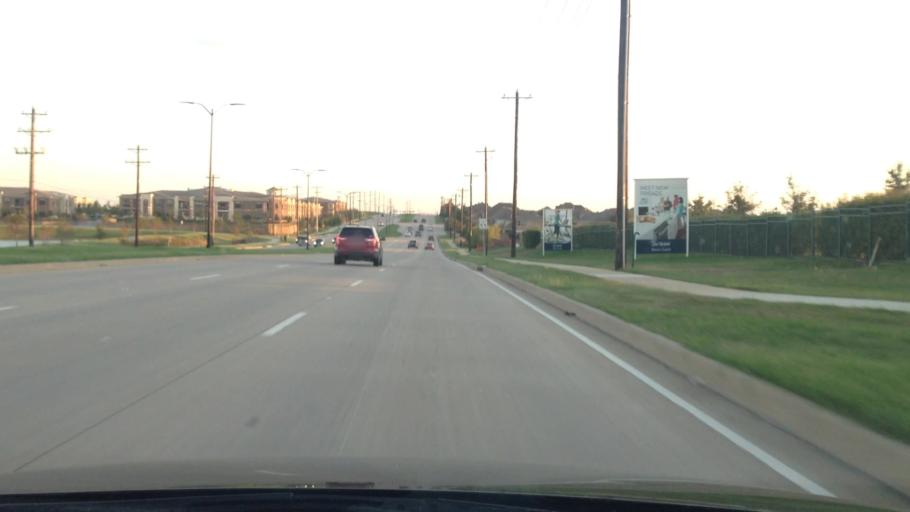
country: US
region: Texas
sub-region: Denton County
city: The Colony
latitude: 33.1356
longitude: -96.8908
